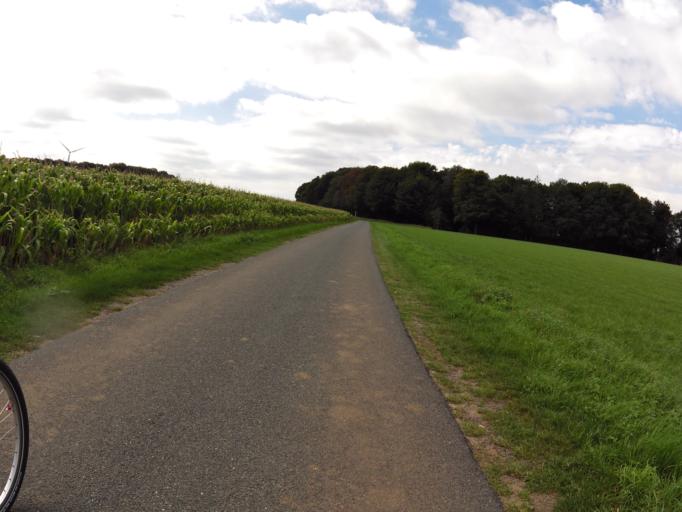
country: DE
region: North Rhine-Westphalia
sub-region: Regierungsbezirk Munster
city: Heek
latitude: 52.1528
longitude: 7.0490
